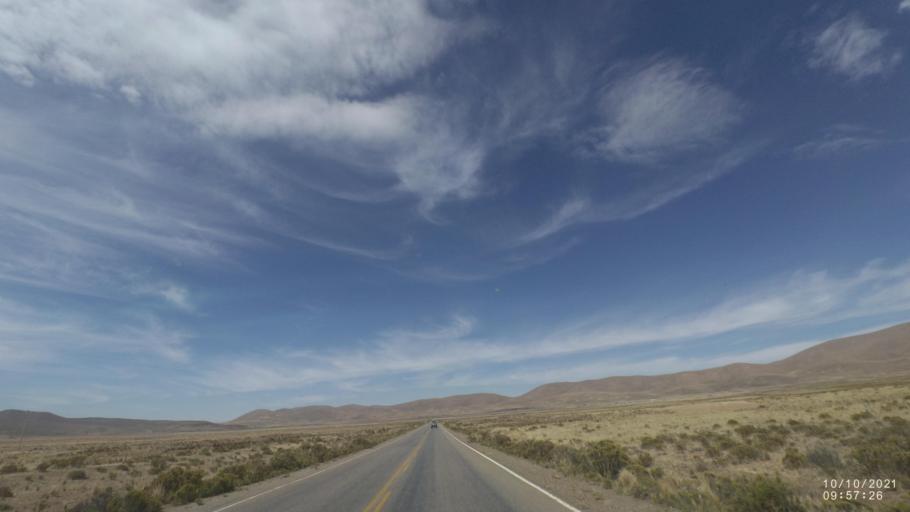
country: BO
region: La Paz
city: Colquiri
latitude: -17.3363
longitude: -67.3850
